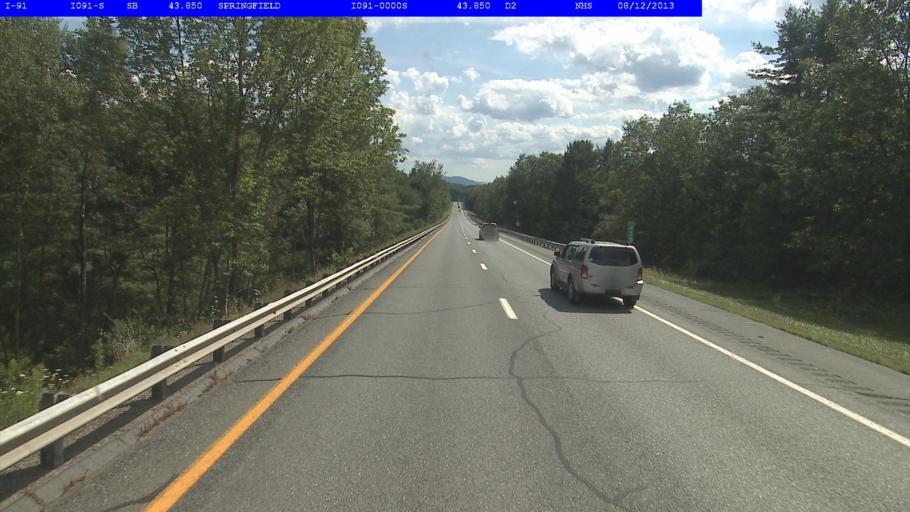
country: US
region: Vermont
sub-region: Windsor County
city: Springfield
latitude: 43.2965
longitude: -72.4273
